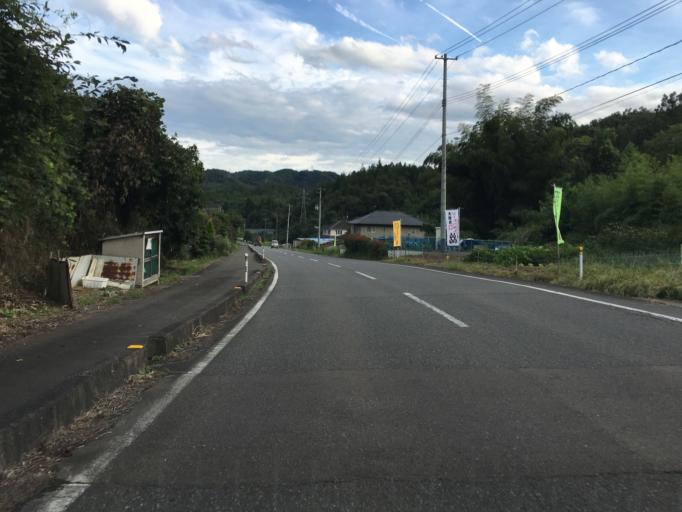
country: JP
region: Fukushima
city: Hobaramachi
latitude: 37.7894
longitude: 140.5425
